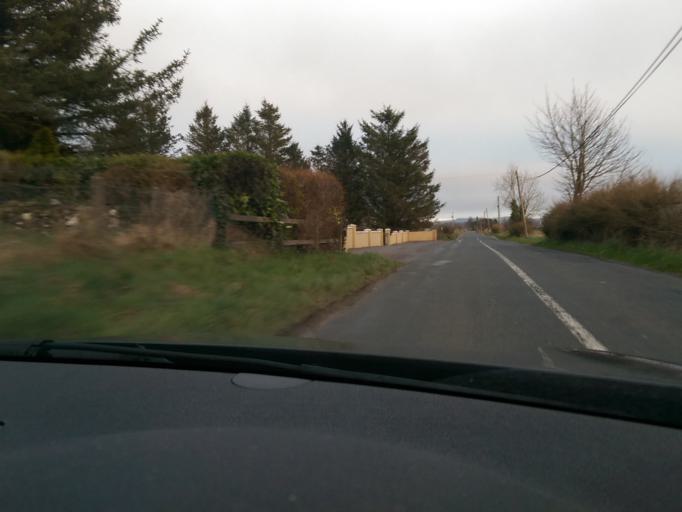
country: IE
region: Connaught
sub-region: Sligo
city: Ballymote
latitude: 54.0197
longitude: -8.5624
